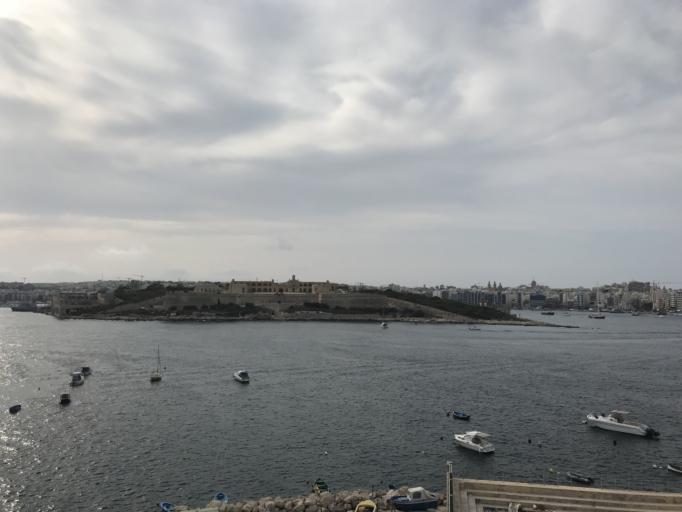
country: MT
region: Il-Furjana
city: Floriana
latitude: 35.9003
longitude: 14.5098
